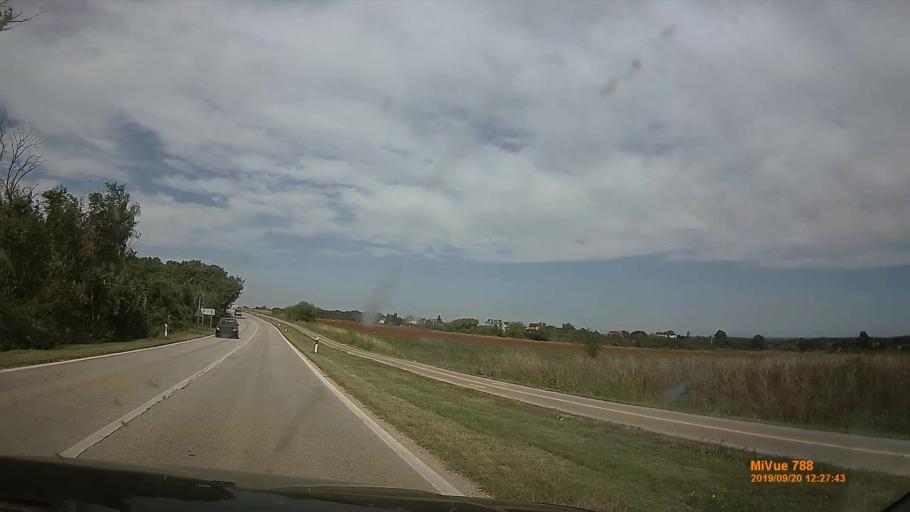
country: HR
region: Istarska
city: Umag
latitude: 45.4092
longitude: 13.5320
